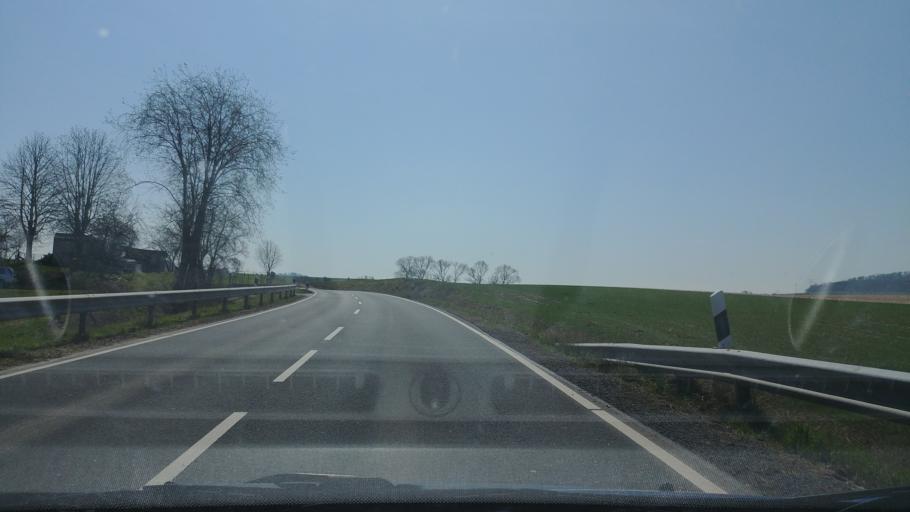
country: DE
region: Lower Saxony
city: Hillerse
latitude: 51.7324
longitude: 9.9380
